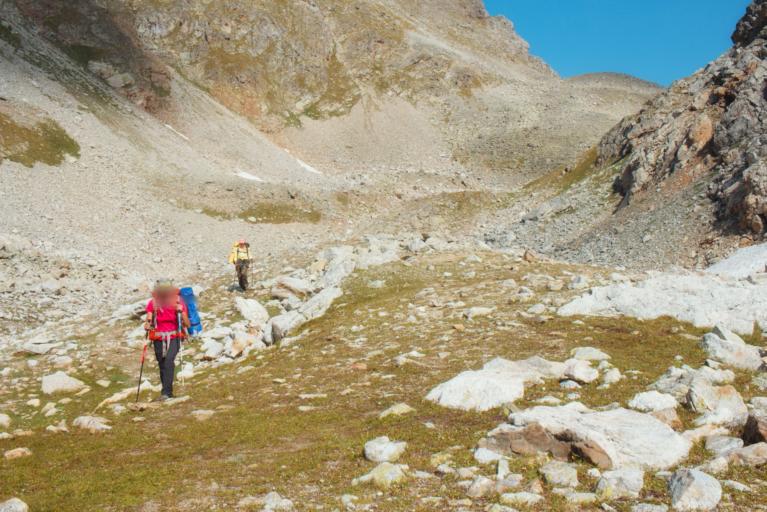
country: RU
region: Karachayevo-Cherkesiya
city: Nizhniy Arkhyz
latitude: 43.4590
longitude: 41.2084
